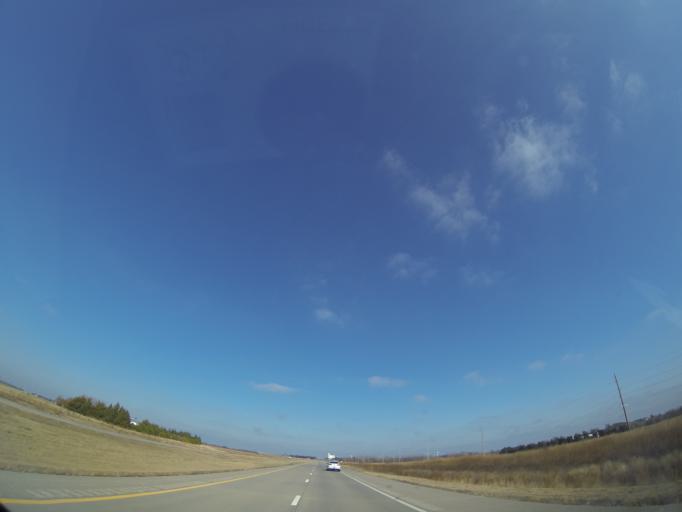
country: US
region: Kansas
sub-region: McPherson County
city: Inman
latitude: 38.2131
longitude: -97.7924
